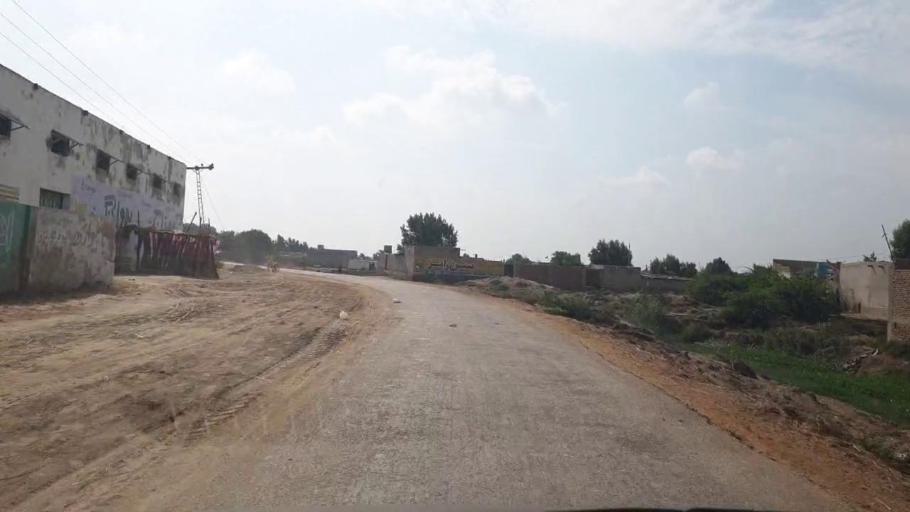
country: PK
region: Sindh
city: Kario
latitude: 24.6467
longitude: 68.5423
